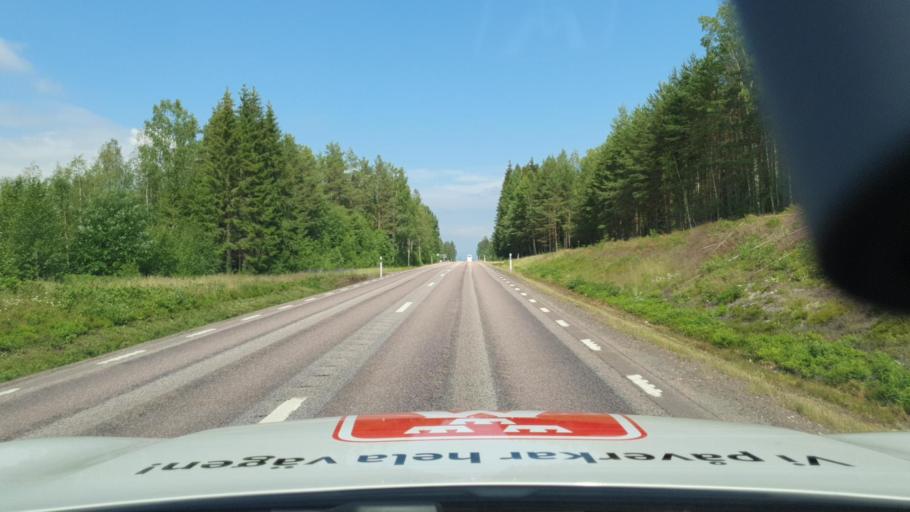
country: SE
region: Vaermland
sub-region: Torsby Kommun
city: Torsby
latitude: 60.0344
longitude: 13.0723
